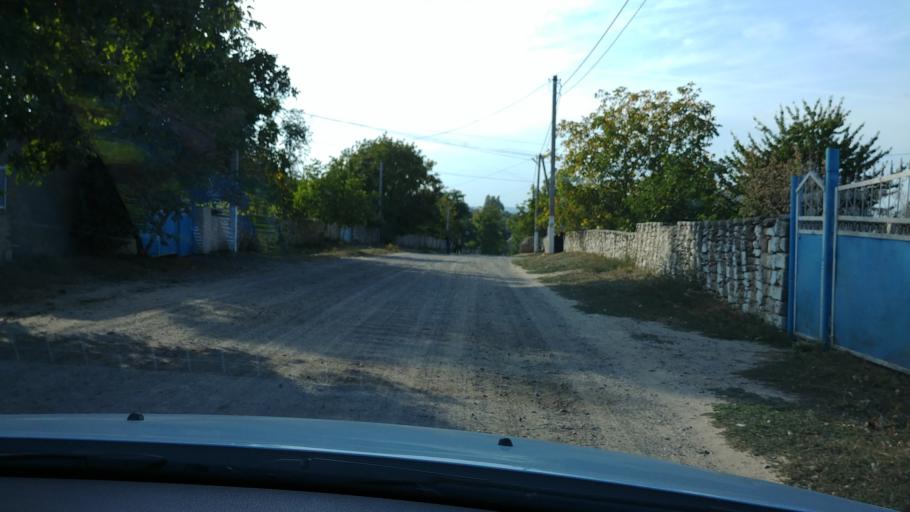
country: MD
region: Rezina
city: Rezina
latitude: 47.7453
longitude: 28.8906
